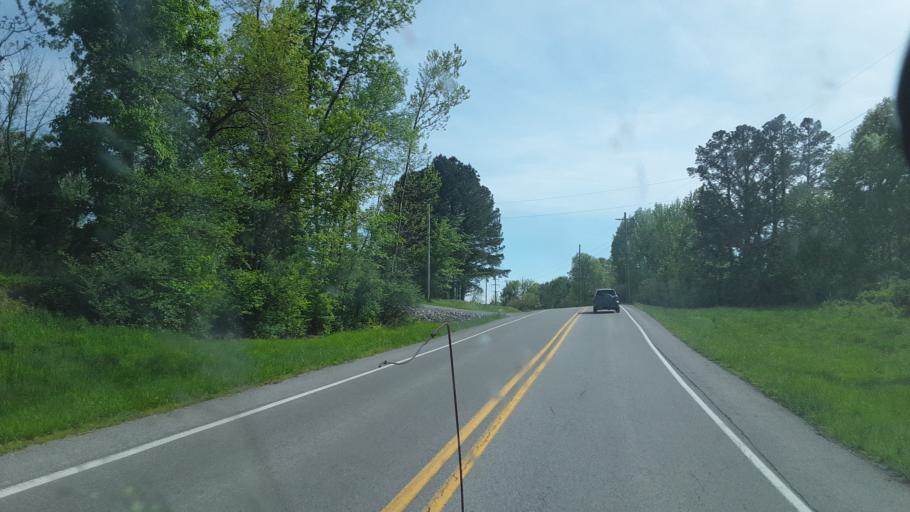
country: US
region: Illinois
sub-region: Jackson County
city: Carbondale
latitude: 37.6812
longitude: -89.2575
